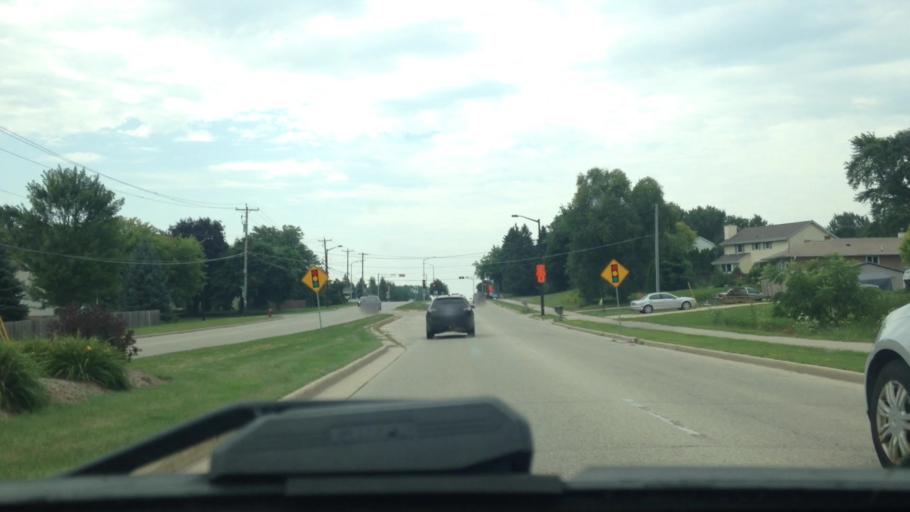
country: US
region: Wisconsin
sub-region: Waukesha County
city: Menomonee Falls
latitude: 43.1360
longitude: -88.1048
